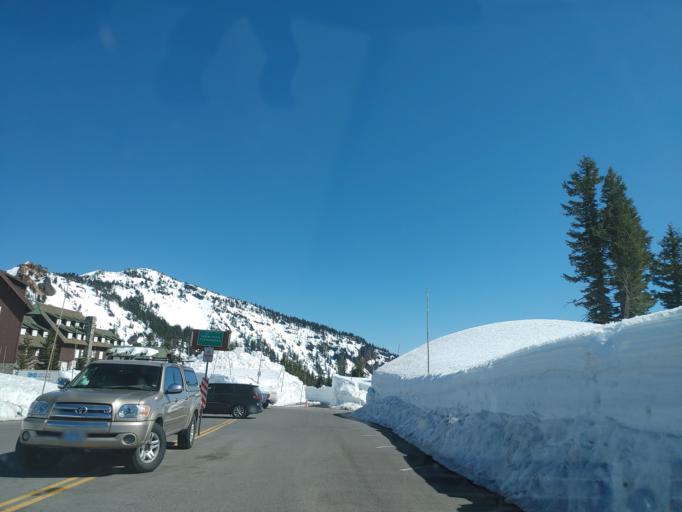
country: US
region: Oregon
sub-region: Jackson County
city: Shady Cove
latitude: 42.9101
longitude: -122.1423
